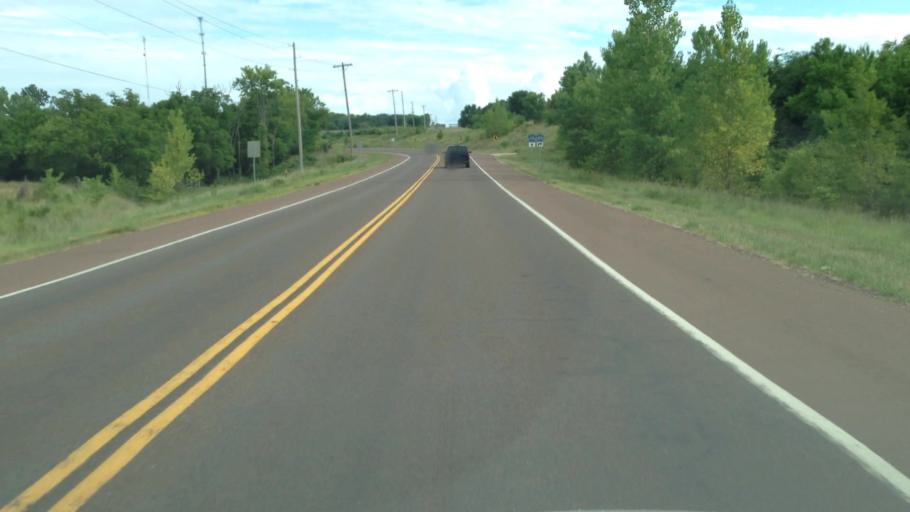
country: US
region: Kansas
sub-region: Douglas County
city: Lawrence
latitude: 39.0051
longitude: -95.3913
